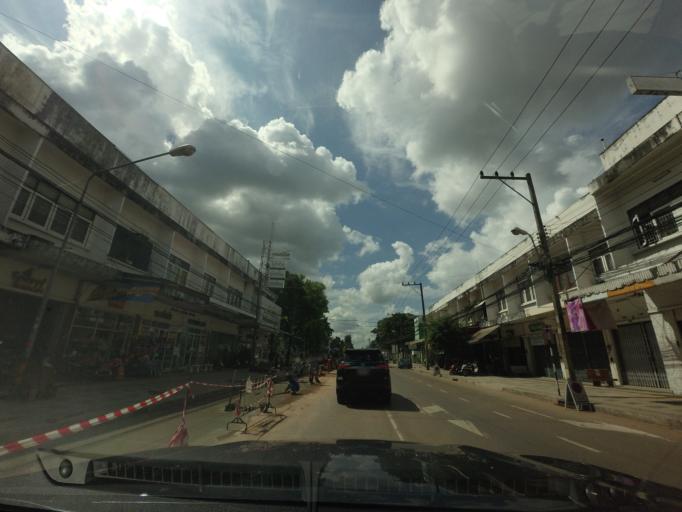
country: TH
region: Changwat Udon Thani
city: Udon Thani
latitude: 17.4060
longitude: 102.7848
